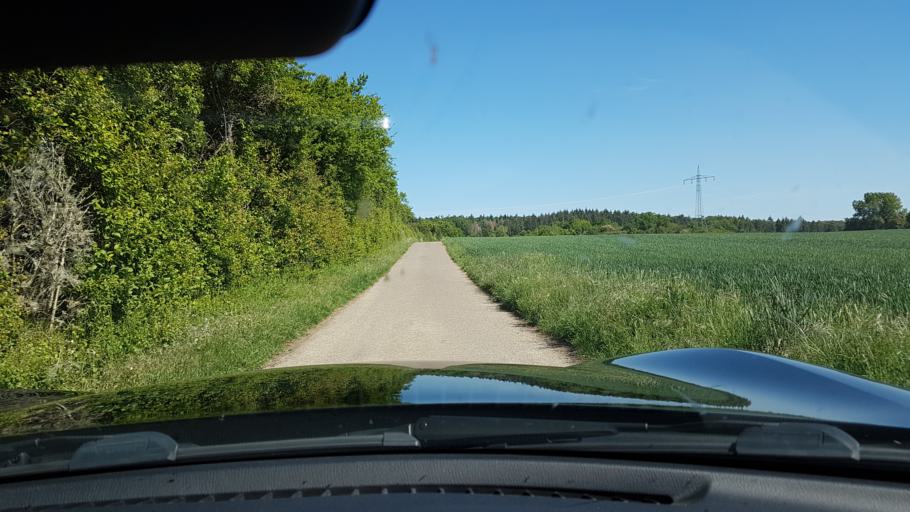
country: DE
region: Baden-Wuerttemberg
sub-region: Karlsruhe Region
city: Osterburken
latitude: 49.4393
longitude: 9.4201
